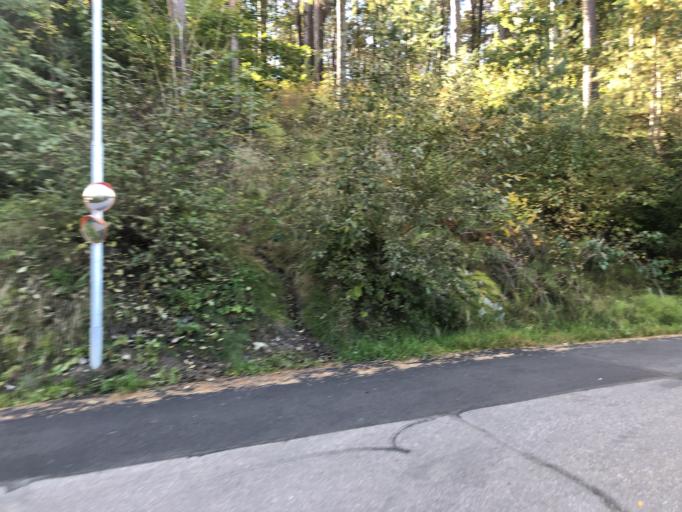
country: SE
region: Vaestra Goetaland
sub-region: Goteborg
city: Majorna
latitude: 57.6330
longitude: 11.9275
